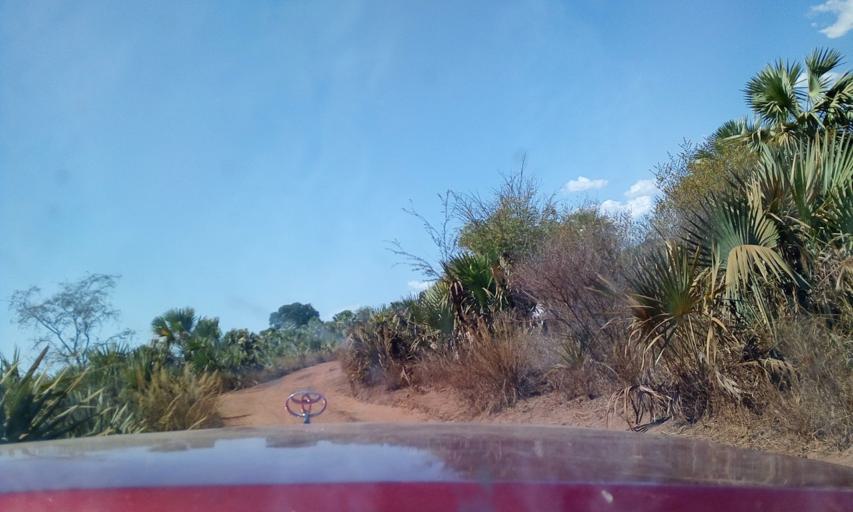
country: MG
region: Boeny
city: Sitampiky
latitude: -16.1254
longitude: 45.4382
